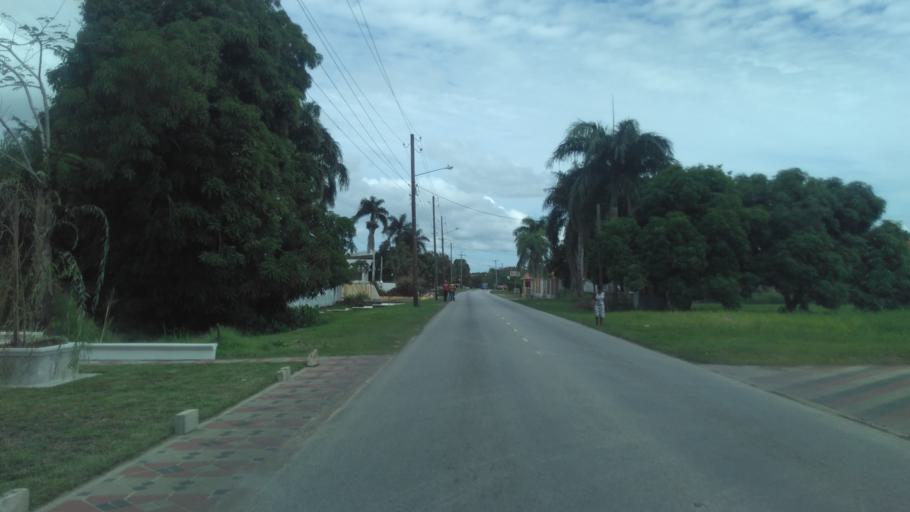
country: SR
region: Paramaribo
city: Paramaribo
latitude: 5.8364
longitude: -55.1257
